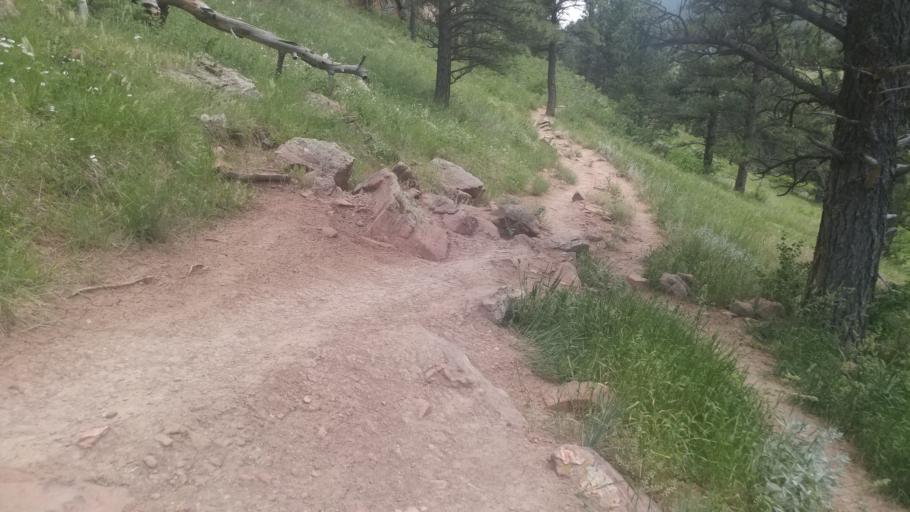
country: US
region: Colorado
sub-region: Boulder County
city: Boulder
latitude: 40.0289
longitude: -105.2960
